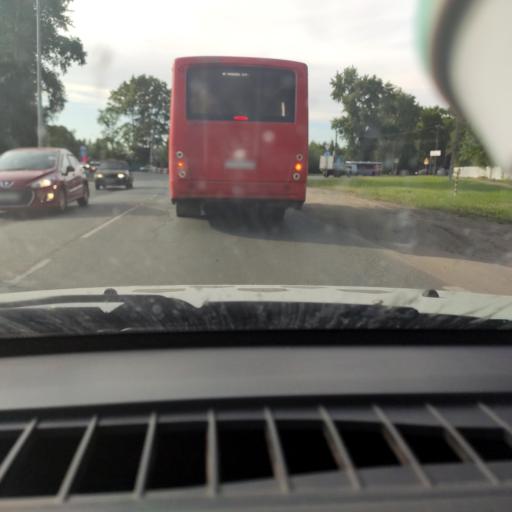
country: RU
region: Kirov
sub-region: Kirovo-Chepetskiy Rayon
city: Kirov
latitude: 58.6145
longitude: 49.7418
